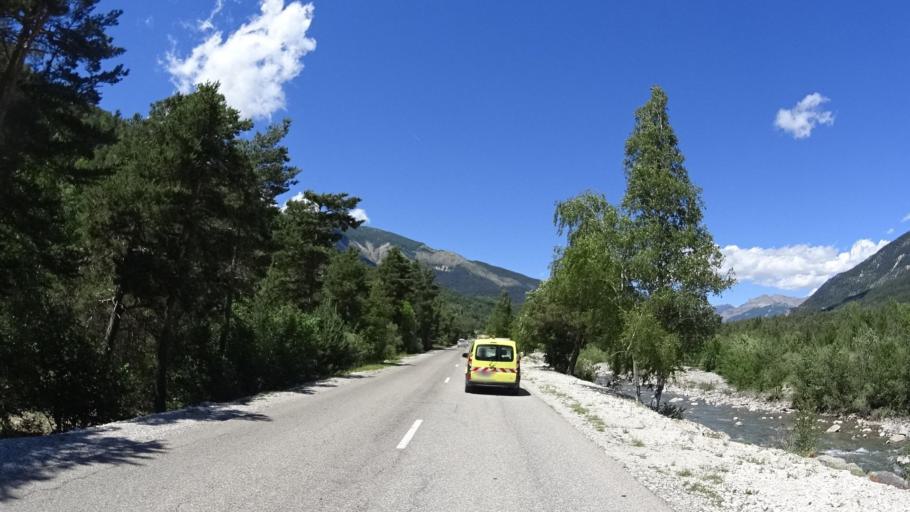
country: FR
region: Provence-Alpes-Cote d'Azur
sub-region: Departement des Alpes-de-Haute-Provence
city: Annot
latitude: 44.1234
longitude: 6.5805
